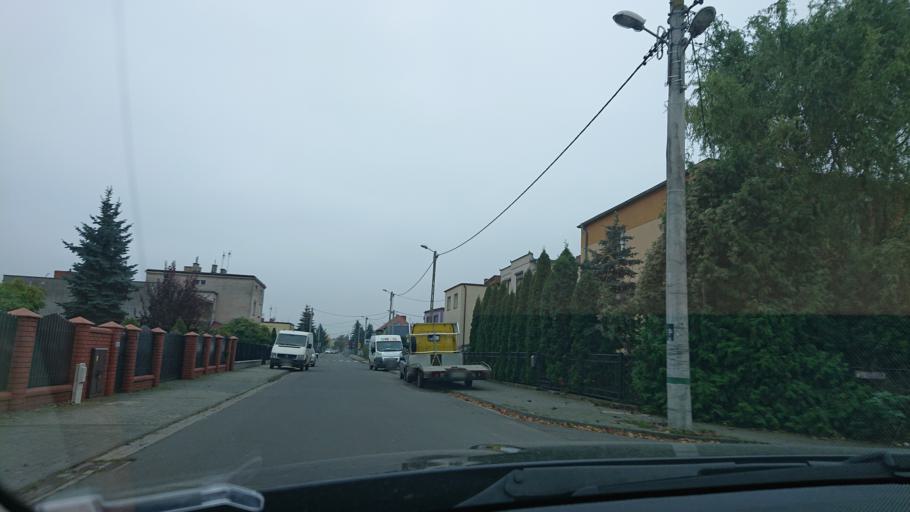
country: PL
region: Greater Poland Voivodeship
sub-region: Powiat gnieznienski
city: Gniezno
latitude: 52.5399
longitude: 17.6236
